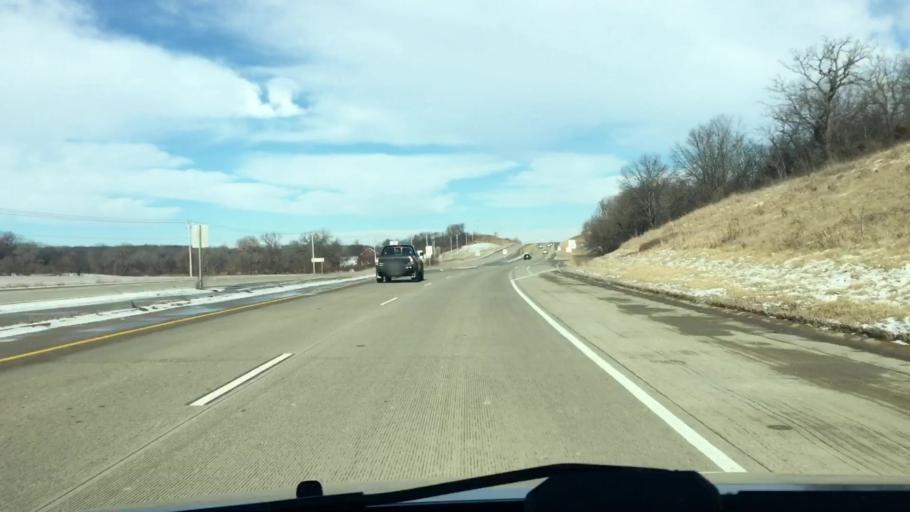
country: US
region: Wisconsin
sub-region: Waukesha County
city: Mukwonago
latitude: 42.9019
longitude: -88.3452
